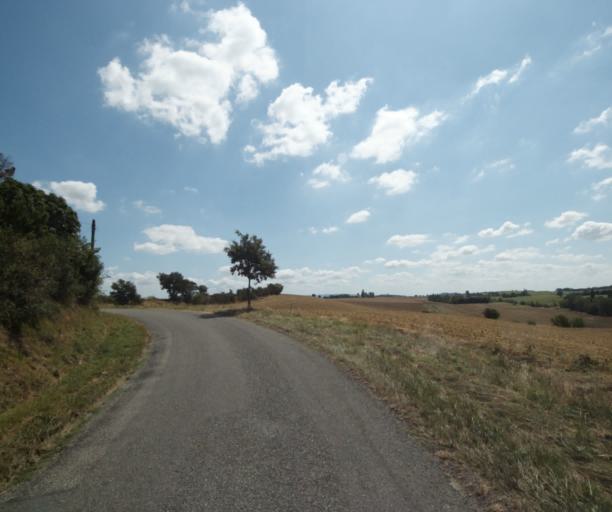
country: FR
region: Midi-Pyrenees
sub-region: Departement de la Haute-Garonne
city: Auriac-sur-Vendinelle
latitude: 43.4762
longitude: 1.8214
